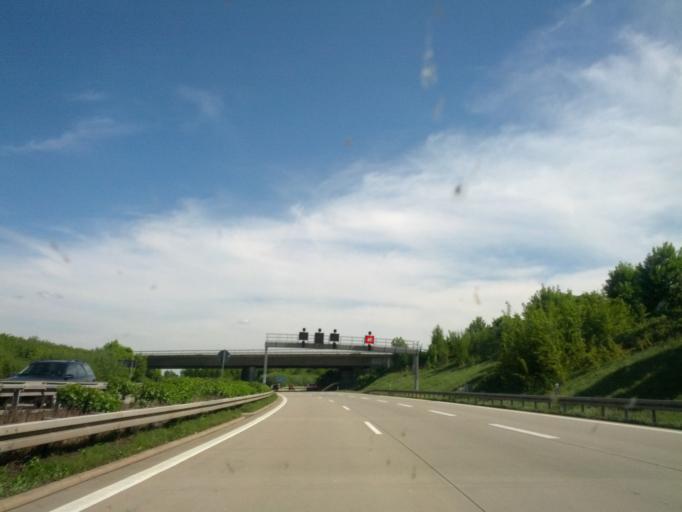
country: DE
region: Saxony
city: Freital
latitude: 51.0390
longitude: 13.6106
